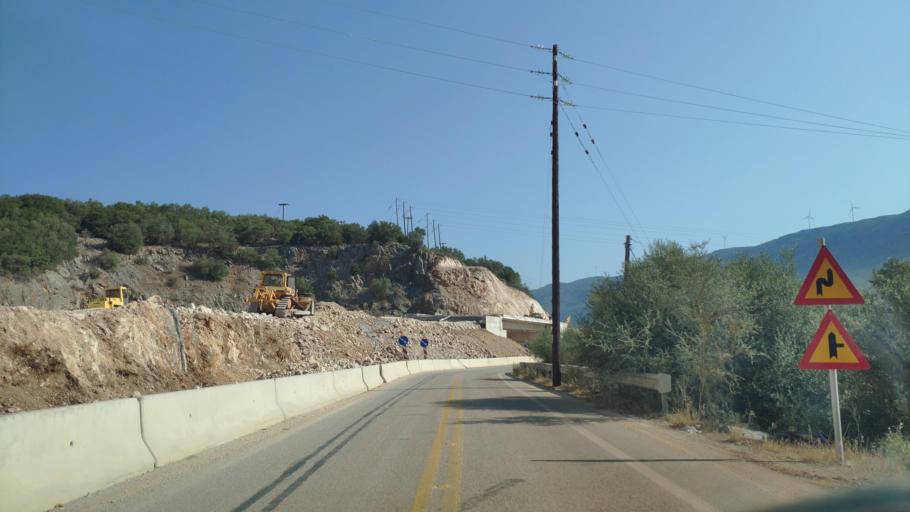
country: GR
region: West Greece
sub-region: Nomos Aitolias kai Akarnanias
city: Stanos
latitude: 38.7772
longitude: 21.1849
